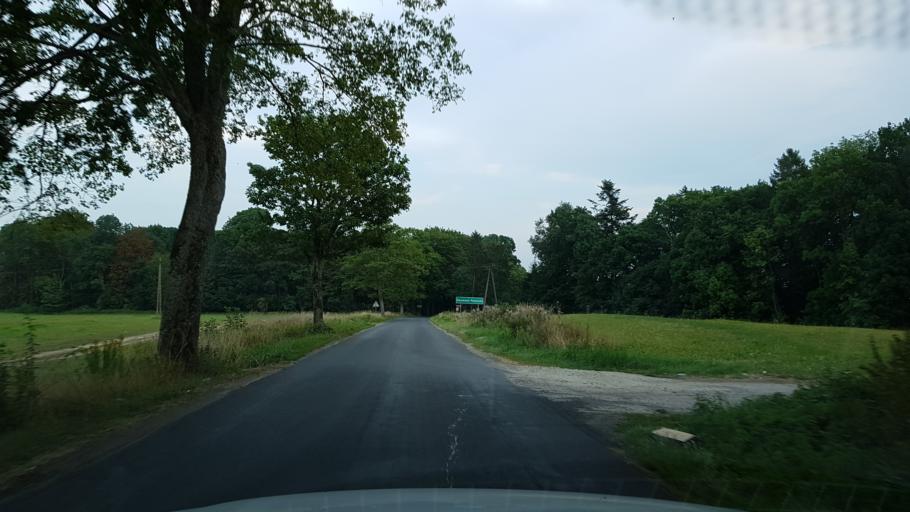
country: PL
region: West Pomeranian Voivodeship
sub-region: Powiat koszalinski
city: Mielno
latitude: 54.2289
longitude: 16.0215
